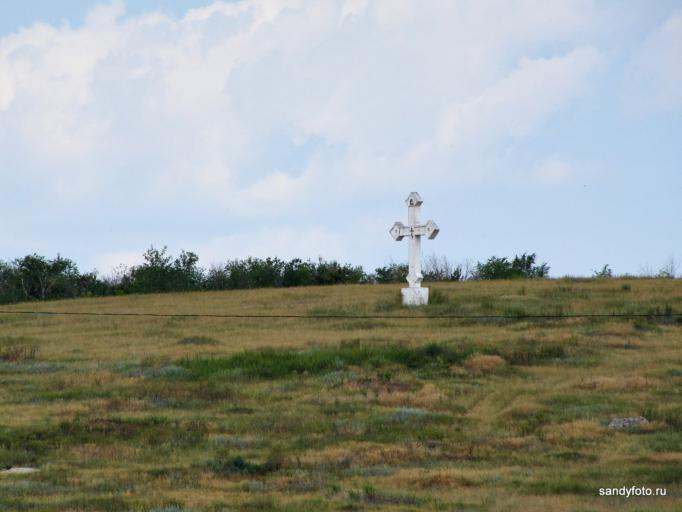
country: RU
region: Chelyabinsk
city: Troitsk
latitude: 54.0939
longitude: 61.5997
